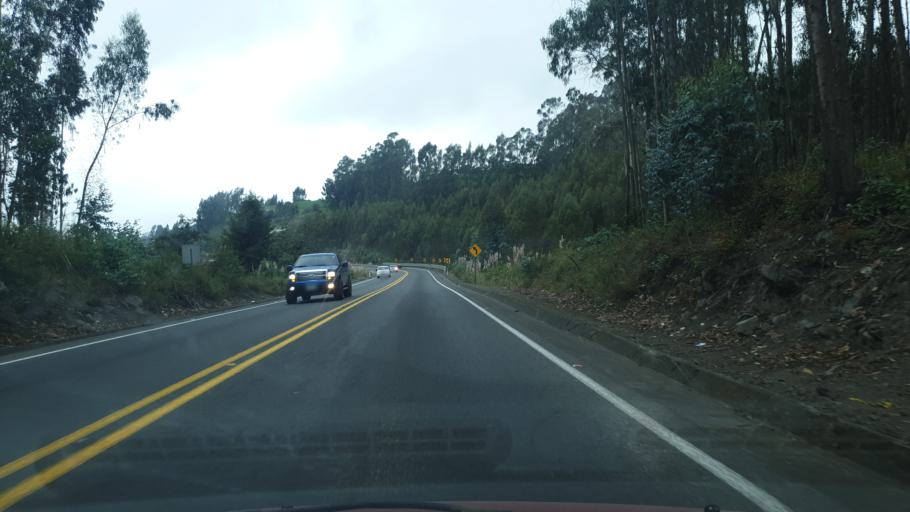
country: EC
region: Tungurahua
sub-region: Canton Quero
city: Quero
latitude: -1.3771
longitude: -78.6503
